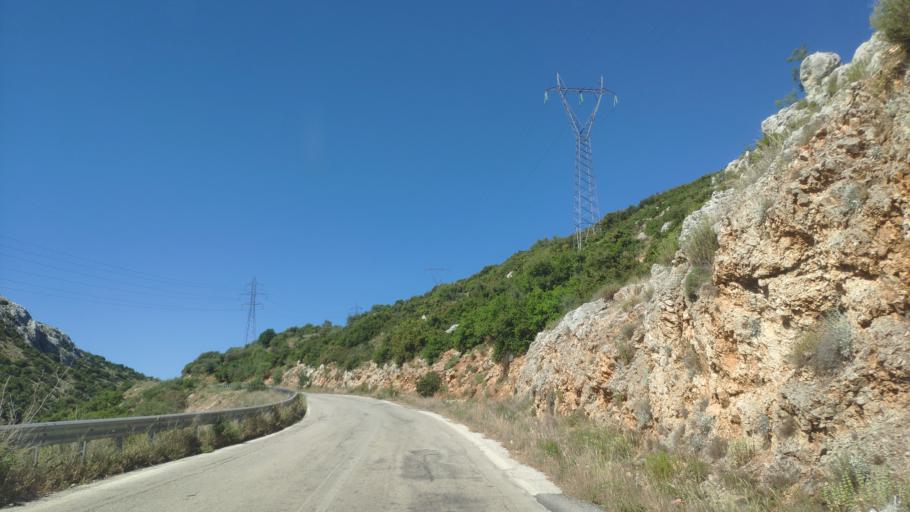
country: GR
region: Peloponnese
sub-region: Nomos Korinthias
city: Khiliomodhi
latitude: 37.7607
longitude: 22.8787
